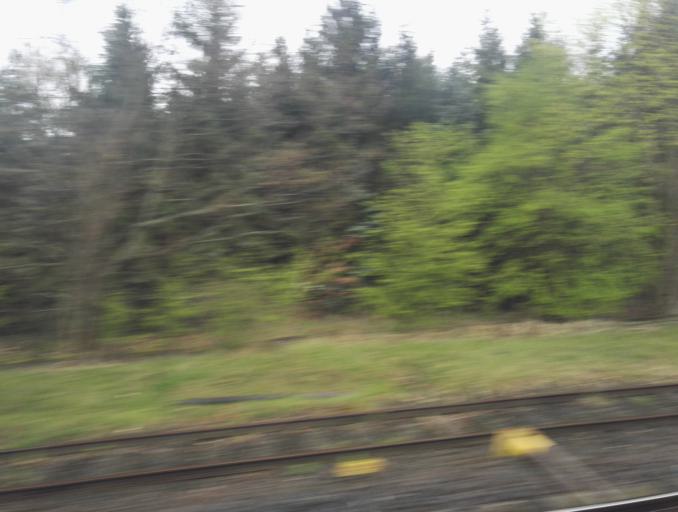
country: DE
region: Lower Saxony
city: Alt Wallmoden
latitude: 52.0387
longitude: 10.3285
